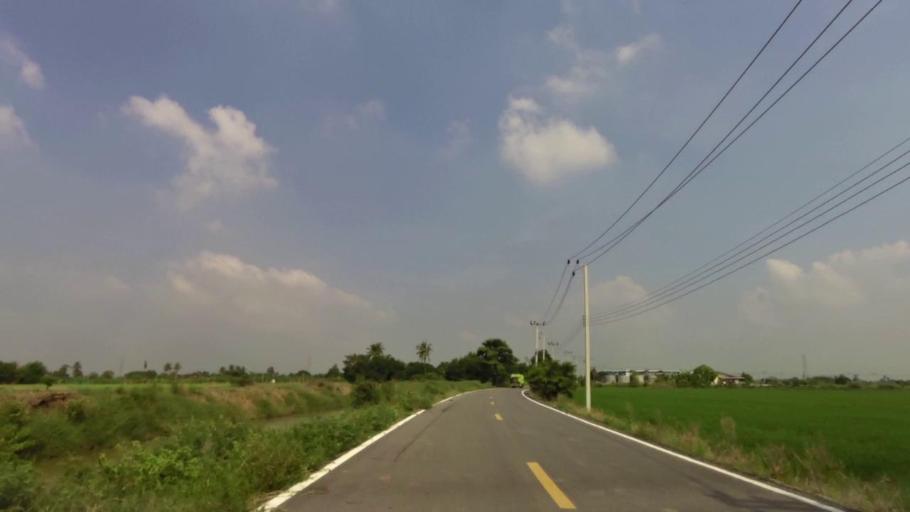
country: TH
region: Ang Thong
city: Pho Thong
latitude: 14.6107
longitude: 100.3978
